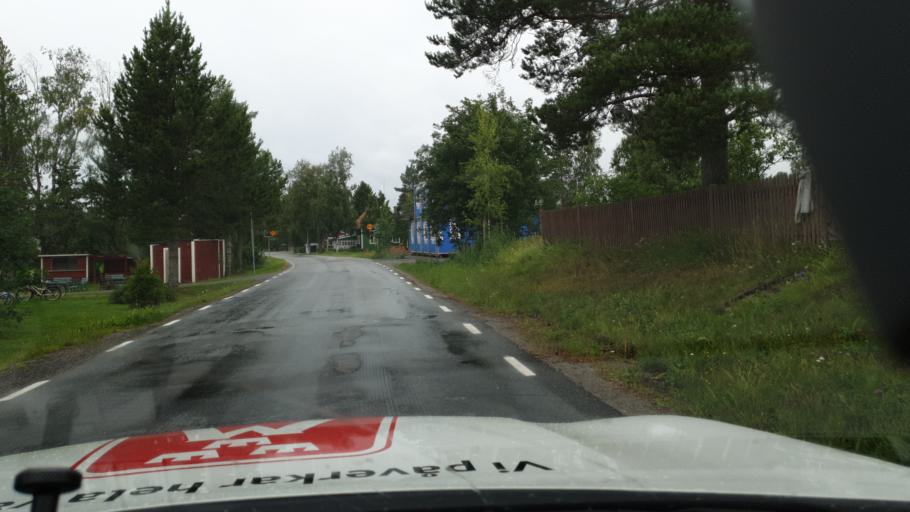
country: SE
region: Vaesterbotten
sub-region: Umea Kommun
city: Saevar
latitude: 64.0321
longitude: 20.4808
